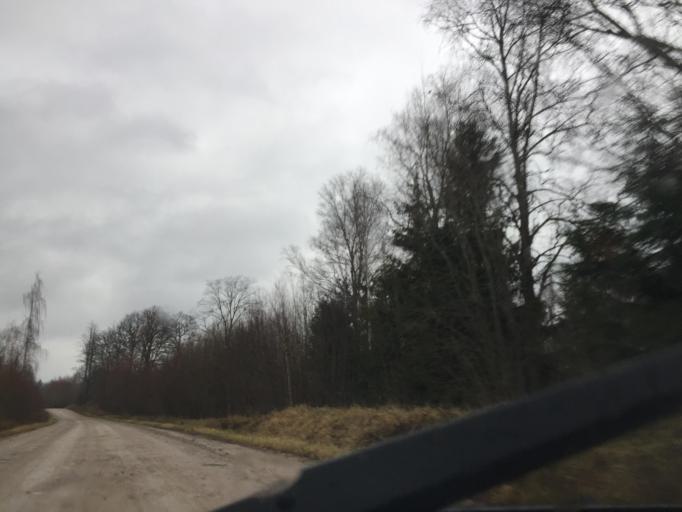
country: LV
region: Limbazu Rajons
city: Limbazi
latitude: 57.6394
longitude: 24.7731
